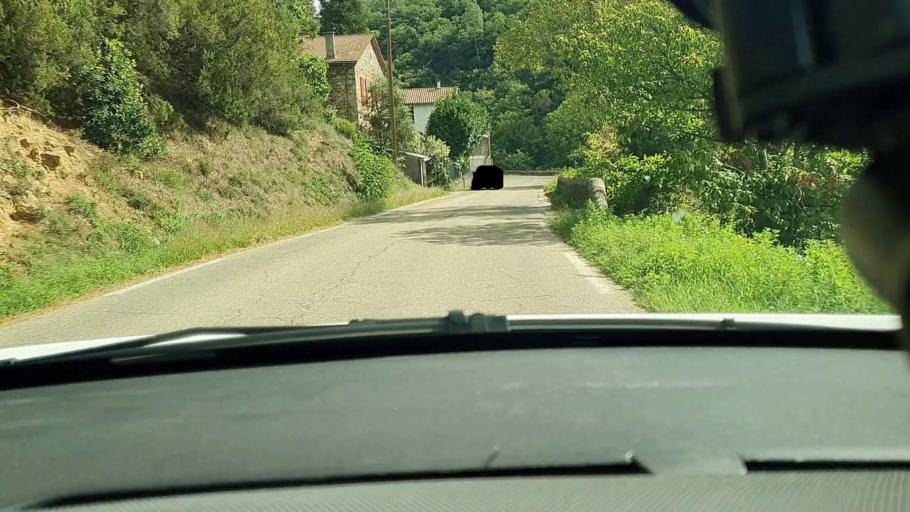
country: FR
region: Languedoc-Roussillon
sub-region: Departement du Gard
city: Branoux-les-Taillades
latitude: 44.2162
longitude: 4.0097
